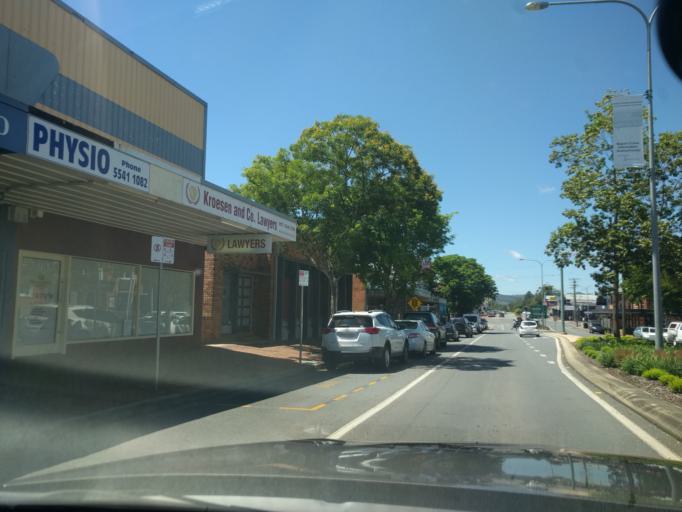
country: AU
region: Queensland
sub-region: Logan
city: Cedar Vale
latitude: -27.9869
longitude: 152.9958
